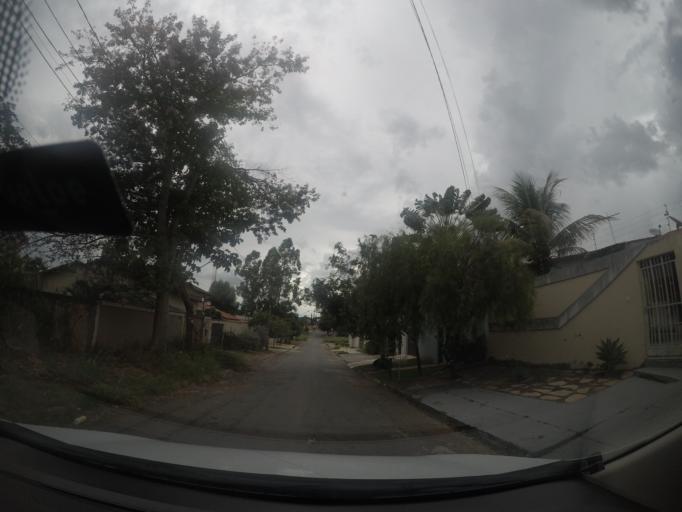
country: BR
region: Goias
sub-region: Goiania
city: Goiania
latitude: -16.6444
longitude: -49.2243
